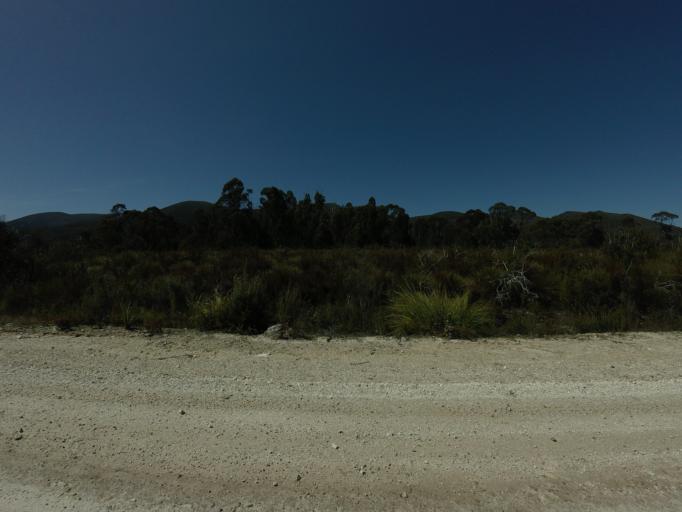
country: AU
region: Tasmania
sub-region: Huon Valley
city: Geeveston
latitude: -43.0261
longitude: 146.3541
